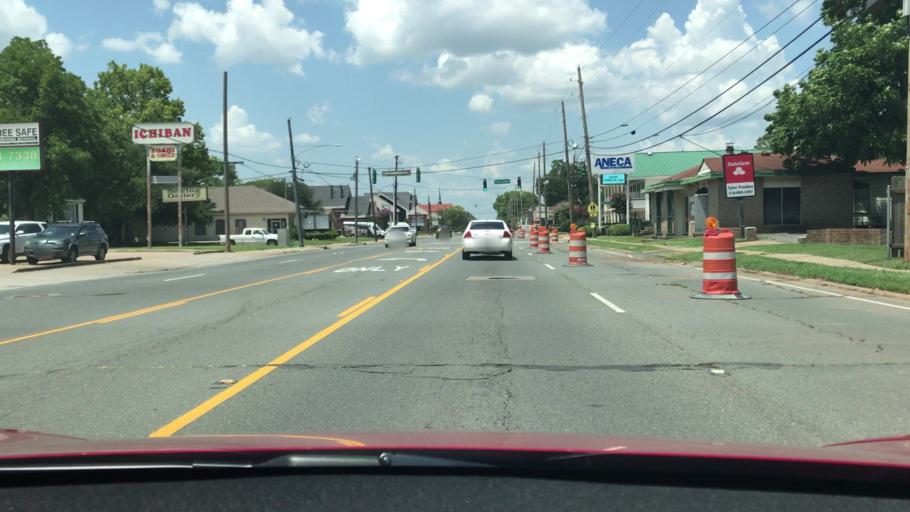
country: US
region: Louisiana
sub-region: Bossier Parish
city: Bossier City
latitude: 32.4596
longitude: -93.7221
